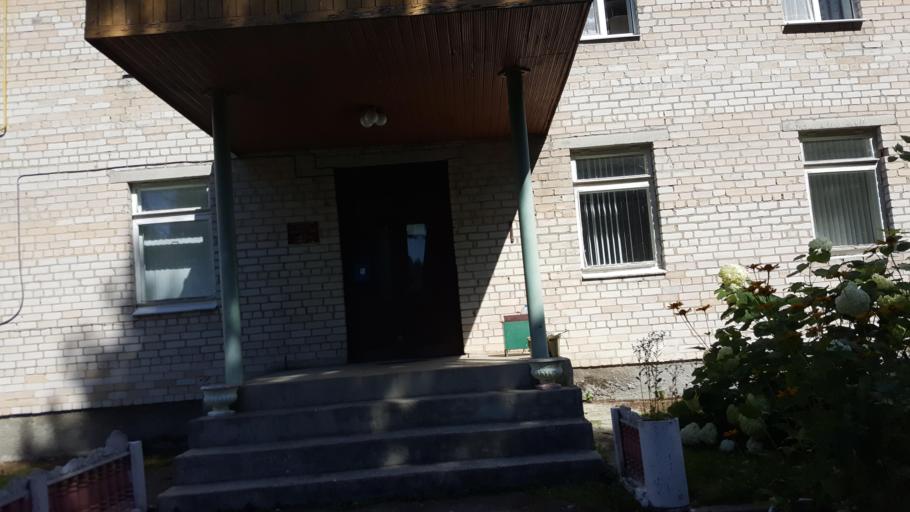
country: BY
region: Brest
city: Charnawchytsy
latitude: 52.2553
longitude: 23.5840
